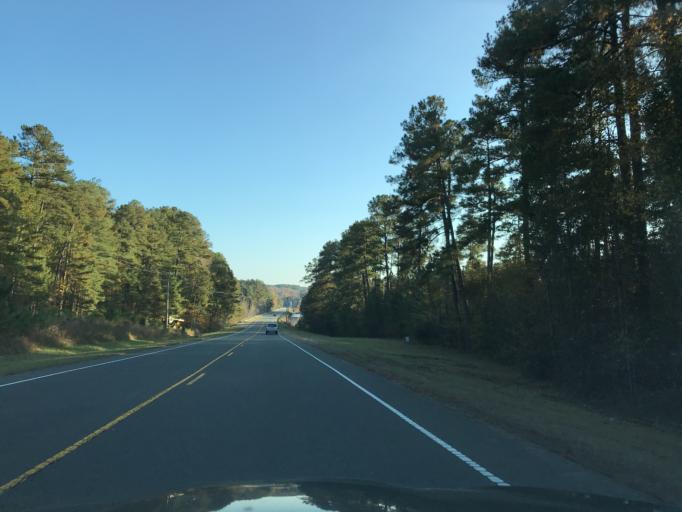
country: US
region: North Carolina
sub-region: Granville County
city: Creedmoor
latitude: 36.0230
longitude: -78.6952
